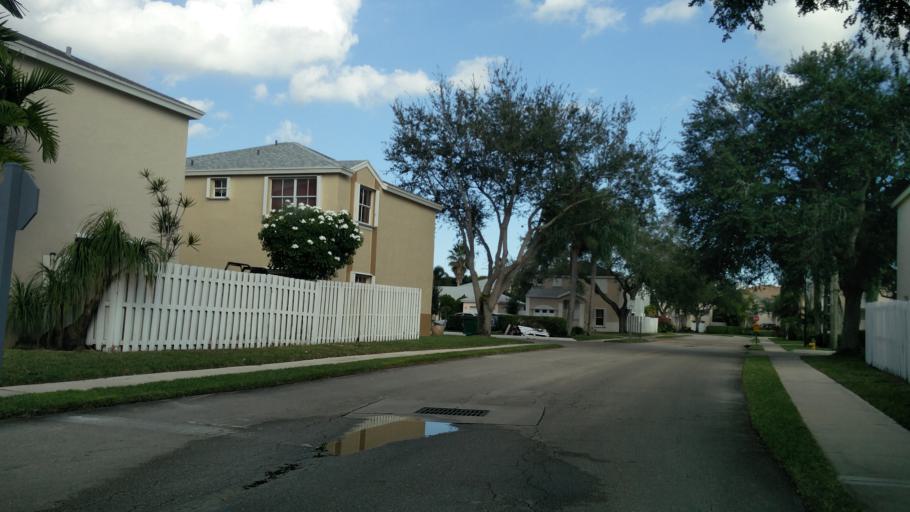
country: US
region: Florida
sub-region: Broward County
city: Davie
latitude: 26.0696
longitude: -80.2422
